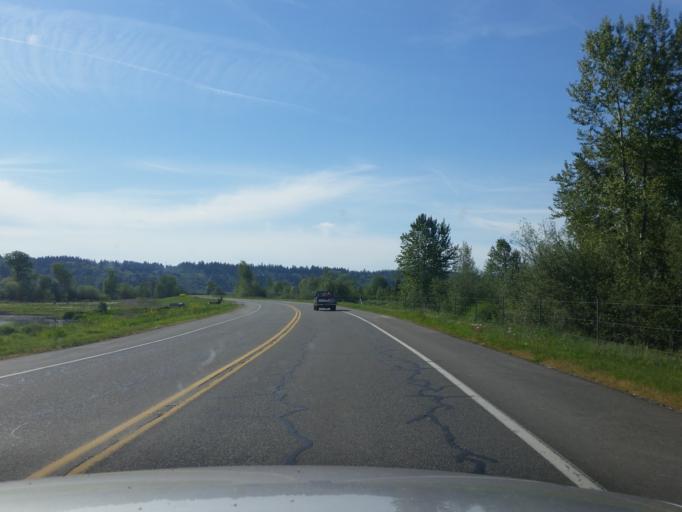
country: US
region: Washington
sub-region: Snohomish County
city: Fobes Hill
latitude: 47.9239
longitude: -122.1563
